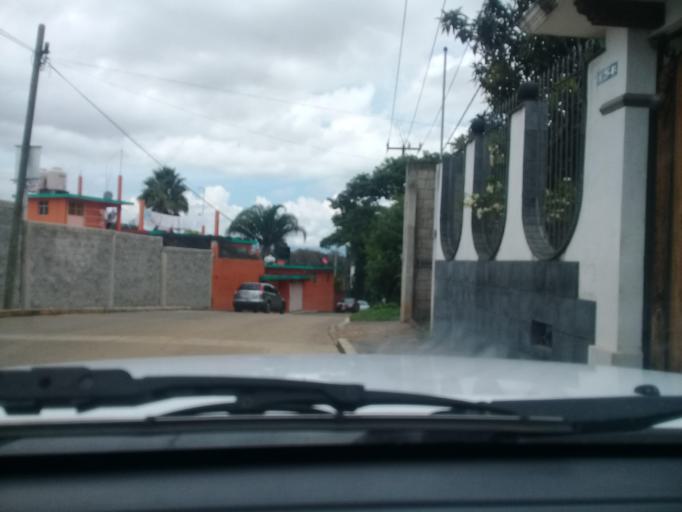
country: MX
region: Veracruz
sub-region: Xalapa
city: Xalapa de Enriquez
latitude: 19.5070
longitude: -96.9139
